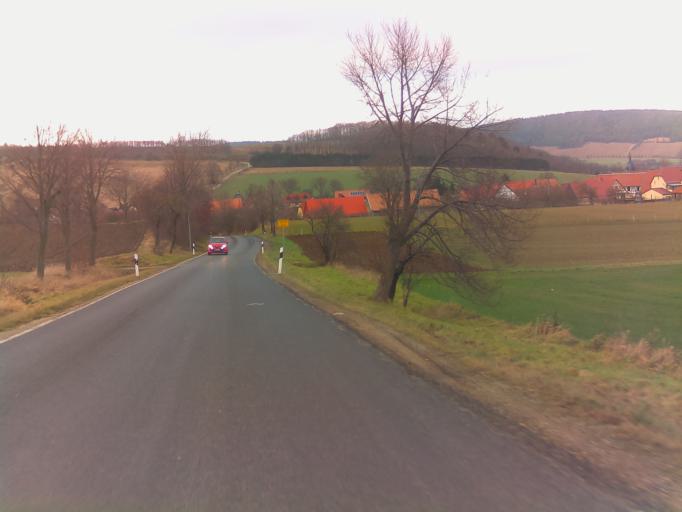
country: DE
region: Thuringia
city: Rottenbach
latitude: 50.7437
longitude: 11.2133
